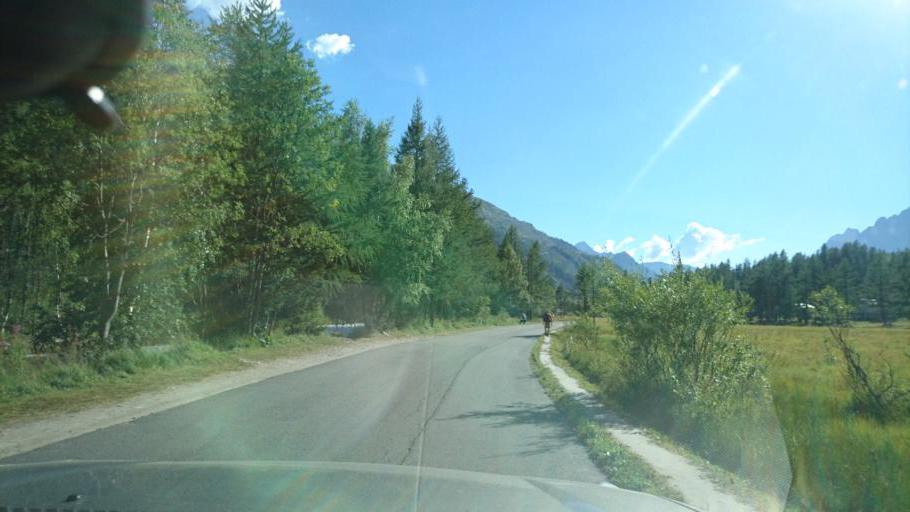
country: IT
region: Aosta Valley
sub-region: Valle d'Aosta
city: Courmayeur
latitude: 45.8459
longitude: 7.0157
